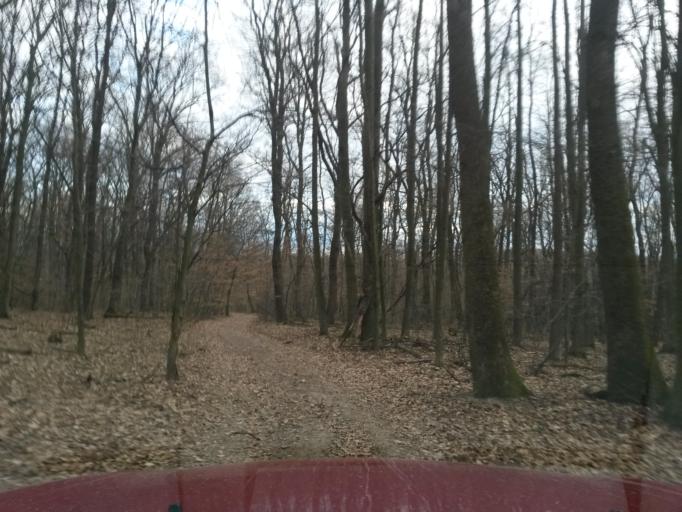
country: SK
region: Kosicky
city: Kosice
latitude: 48.6971
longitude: 21.2982
